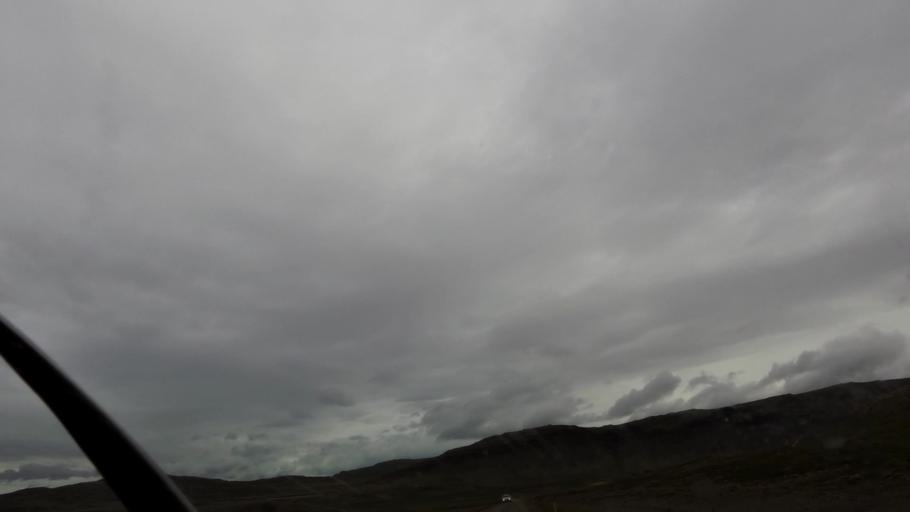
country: IS
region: West
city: Stykkisholmur
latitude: 65.0142
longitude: -22.5743
